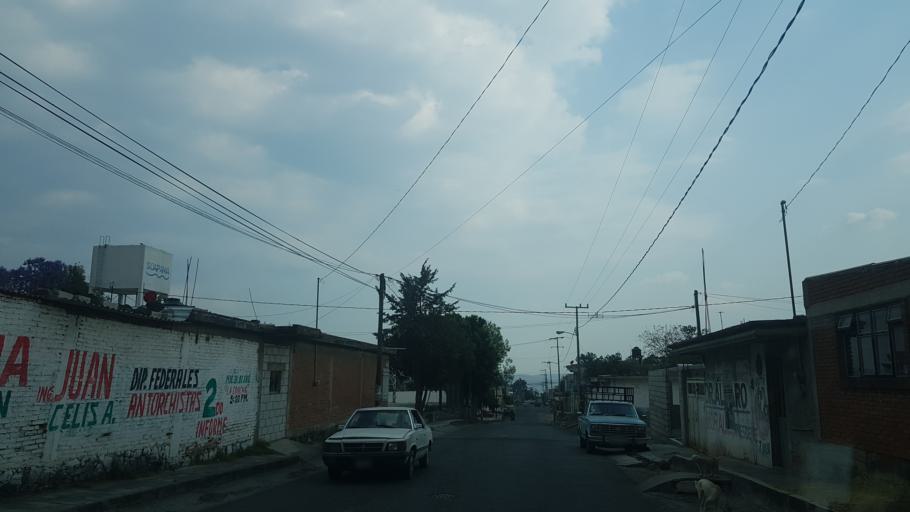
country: MX
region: Puebla
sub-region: Santa Isabel Cholula
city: Santa Ana Acozautla
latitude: 18.9477
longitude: -98.3950
